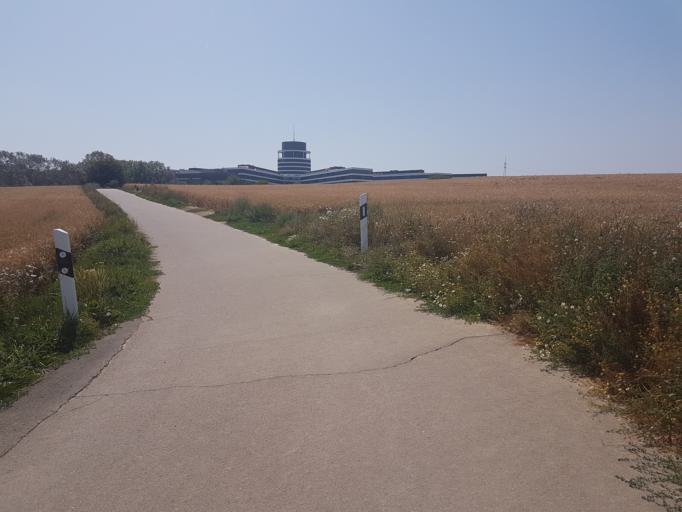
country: LU
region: Luxembourg
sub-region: Canton de Luxembourg
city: Luxembourg
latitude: 49.5835
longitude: 6.1106
